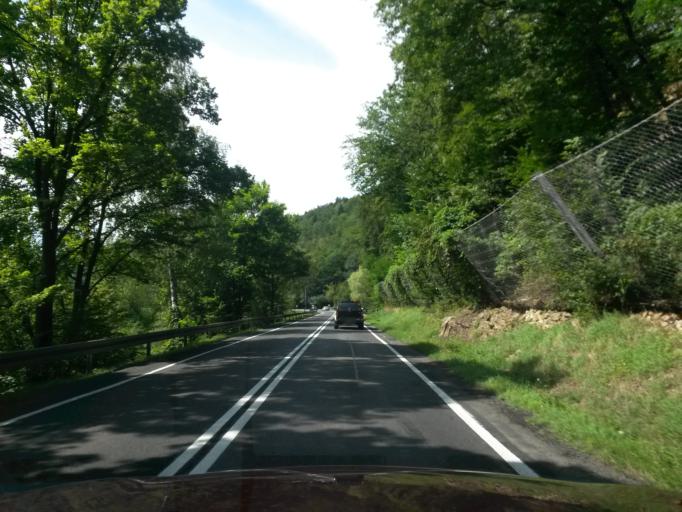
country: PL
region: Lesser Poland Voivodeship
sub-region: Powiat brzeski
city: Czchow
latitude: 49.8096
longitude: 20.6625
